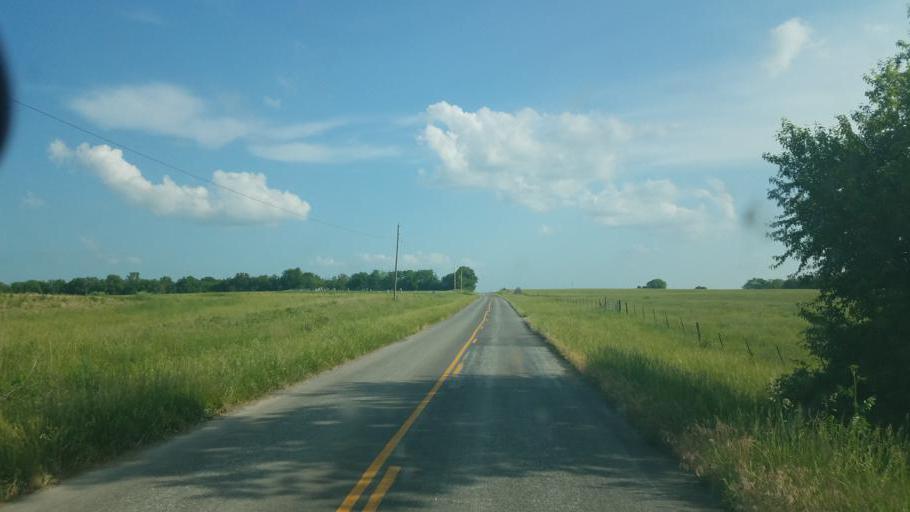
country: US
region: Missouri
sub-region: Moniteau County
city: California
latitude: 38.7883
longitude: -92.6053
